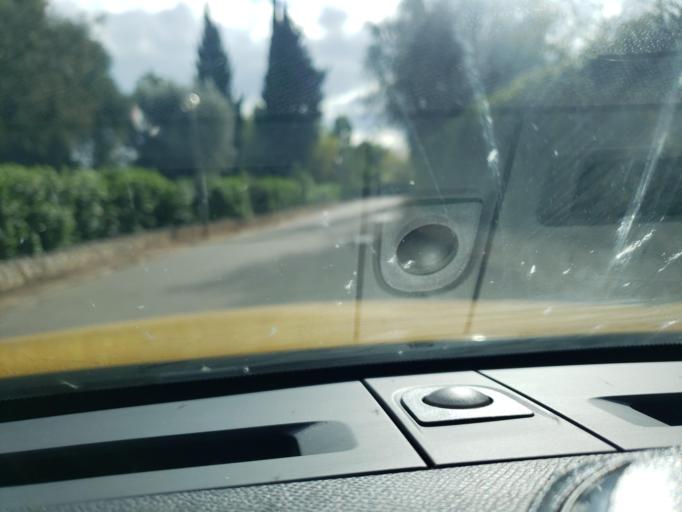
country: PT
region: Faro
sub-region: Portimao
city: Alvor
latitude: 37.1873
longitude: -8.5855
